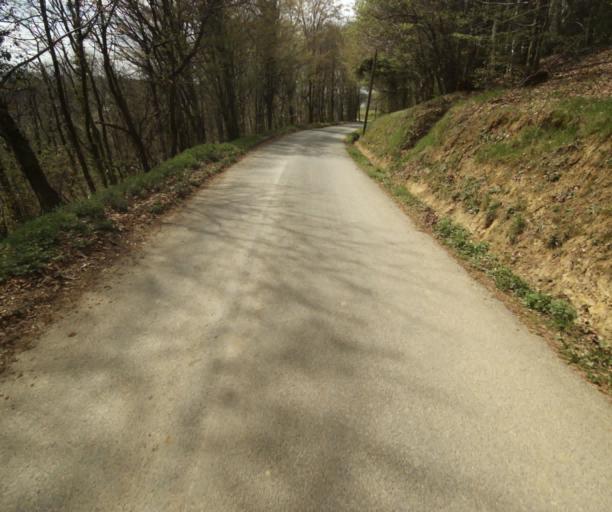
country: FR
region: Limousin
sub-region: Departement de la Correze
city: Naves
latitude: 45.3197
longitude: 1.7716
